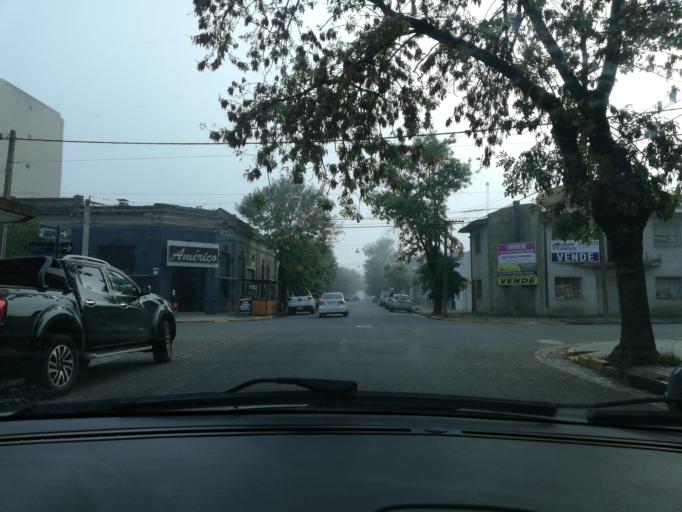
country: AR
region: Buenos Aires
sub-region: Partido de Balcarce
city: Balcarce
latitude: -37.8458
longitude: -58.2526
